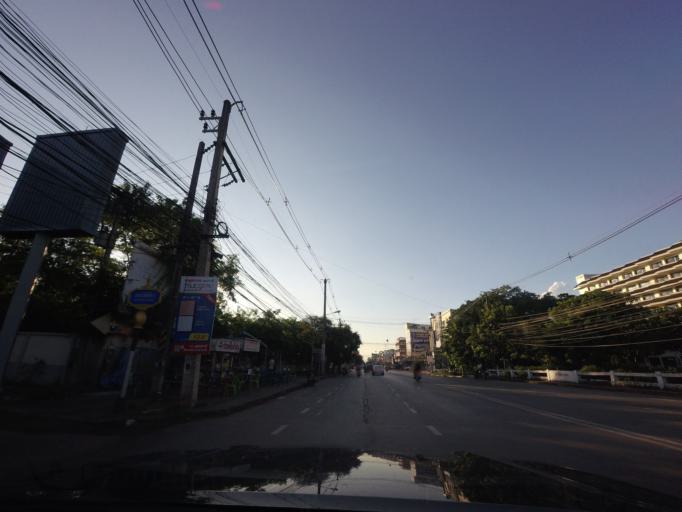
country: TH
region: Changwat Udon Thani
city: Udon Thani
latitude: 17.4009
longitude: 102.8001
